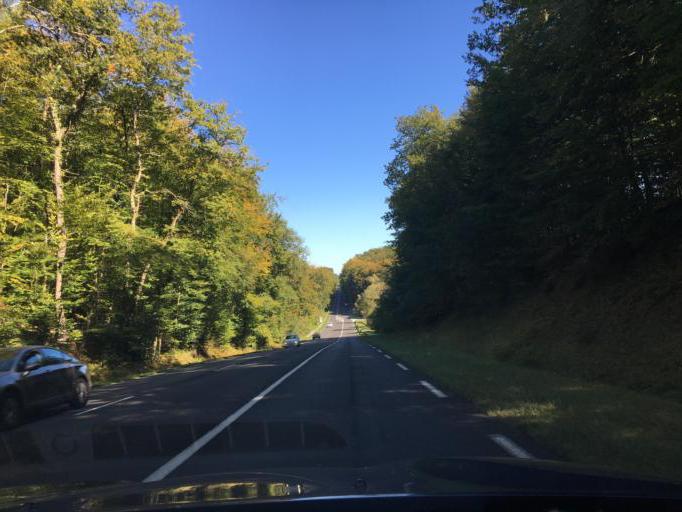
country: FR
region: Centre
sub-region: Departement d'Indre-et-Loire
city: Cheille
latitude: 47.2437
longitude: 0.4338
